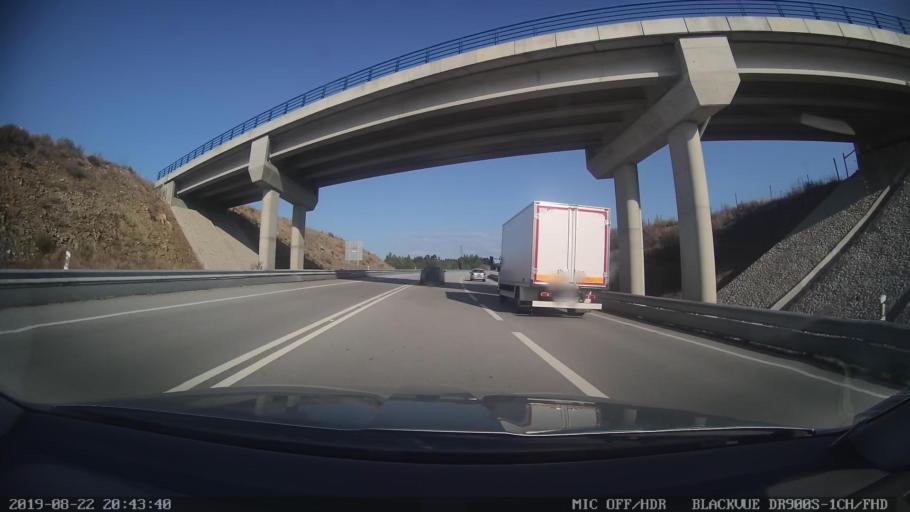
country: PT
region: Castelo Branco
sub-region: Proenca-A-Nova
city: Proenca-a-Nova
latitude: 39.7002
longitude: -7.8364
